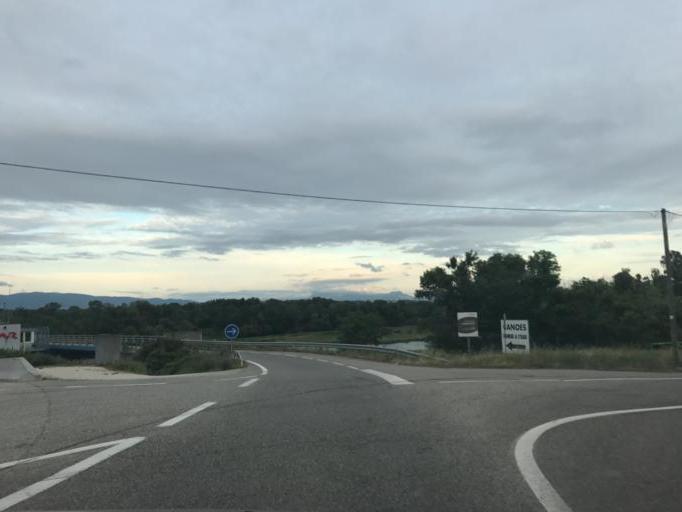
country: FR
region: Rhone-Alpes
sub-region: Departement de l'Ardeche
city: Charmes-sur-Rhone
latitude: 44.8531
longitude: 4.8410
